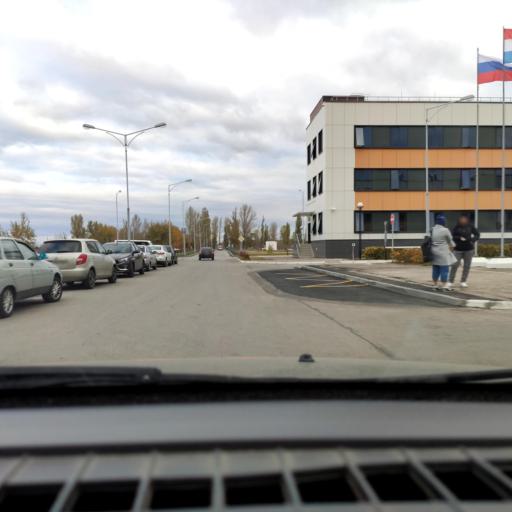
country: RU
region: Samara
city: Podstepki
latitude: 53.5565
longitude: 49.2156
